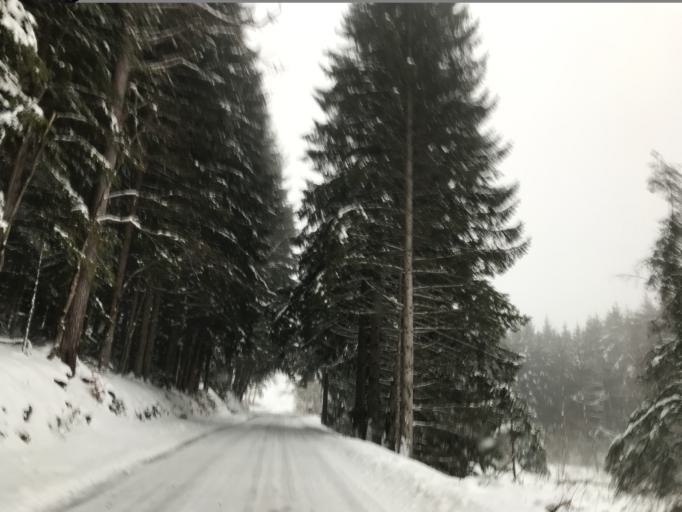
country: FR
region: Auvergne
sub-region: Departement du Puy-de-Dome
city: Job
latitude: 45.7195
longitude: 3.6976
